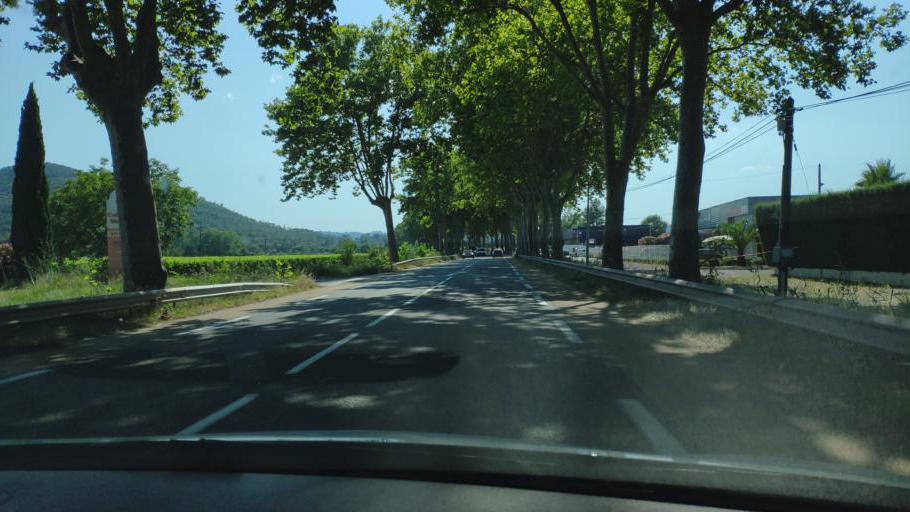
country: FR
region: Provence-Alpes-Cote d'Azur
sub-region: Departement du Var
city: Les Arcs
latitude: 43.4423
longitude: 6.4598
